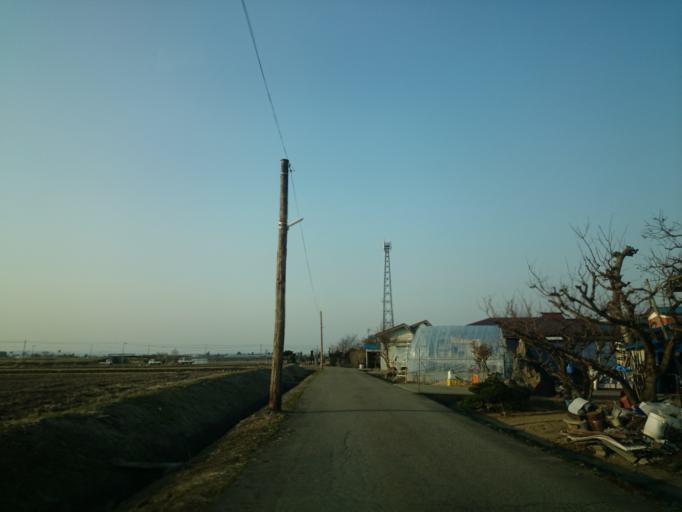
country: JP
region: Fukushima
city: Kitakata
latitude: 37.4421
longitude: 139.8588
